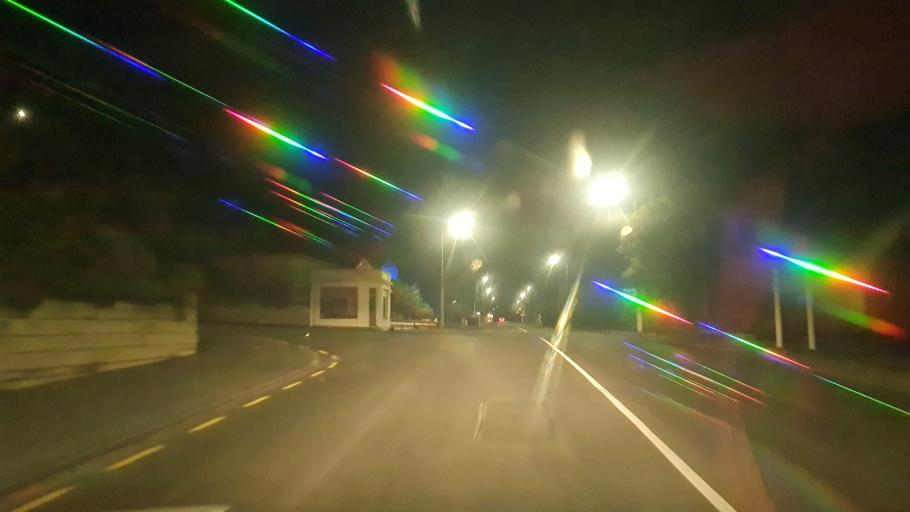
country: NZ
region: Otago
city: Oamaru
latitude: -45.1017
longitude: 170.9676
